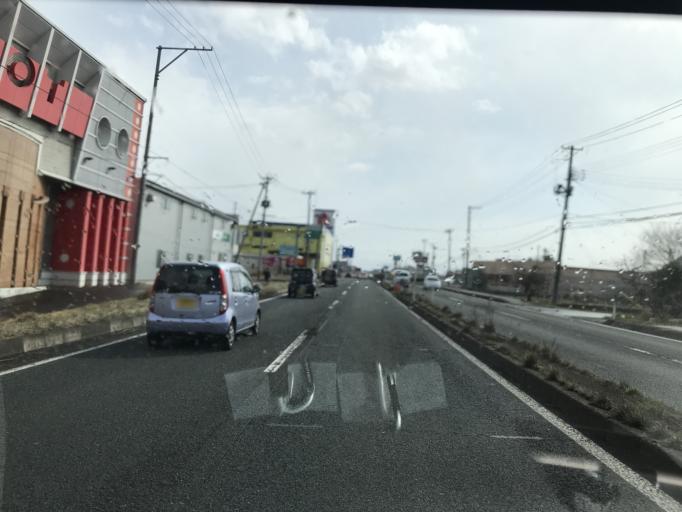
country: JP
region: Iwate
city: Kitakami
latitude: 39.3021
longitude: 141.1081
